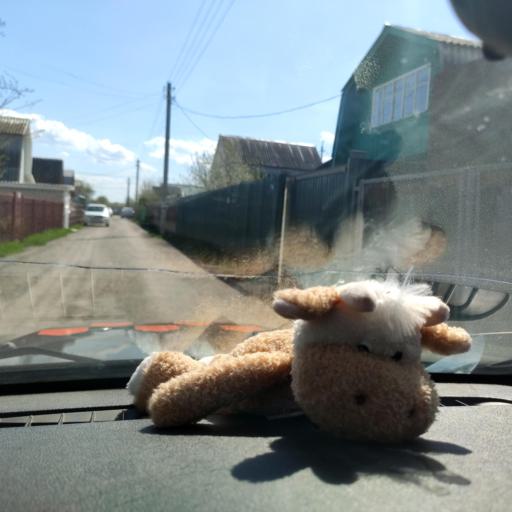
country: RU
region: Samara
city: Podstepki
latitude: 53.5989
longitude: 49.2178
